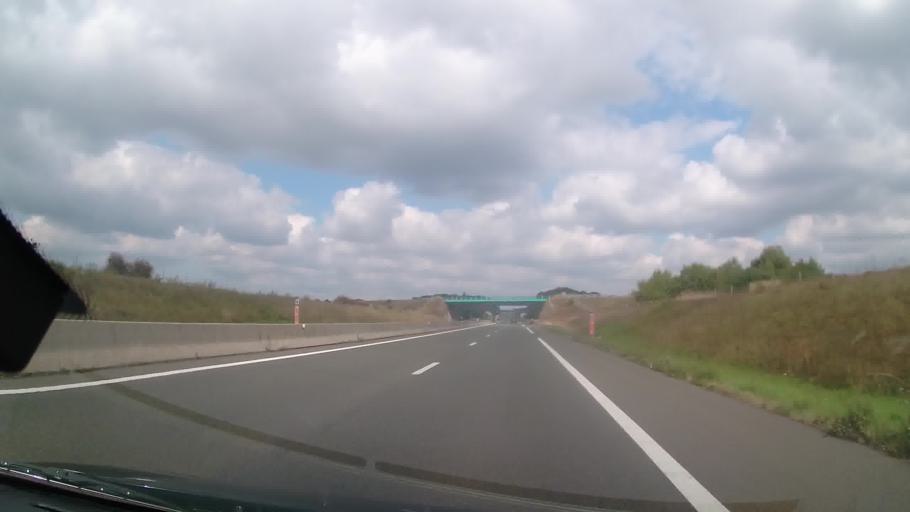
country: FR
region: Picardie
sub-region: Departement de la Somme
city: Nouvion
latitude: 50.2354
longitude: 1.7520
